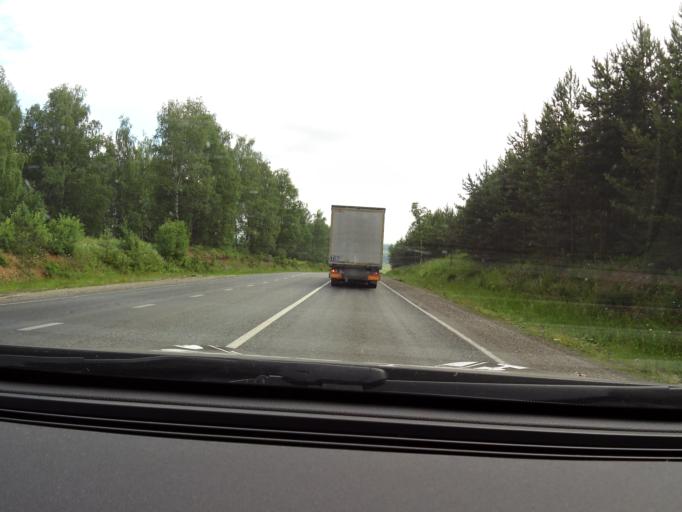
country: RU
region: Perm
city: Suksun
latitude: 57.0844
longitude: 57.4014
